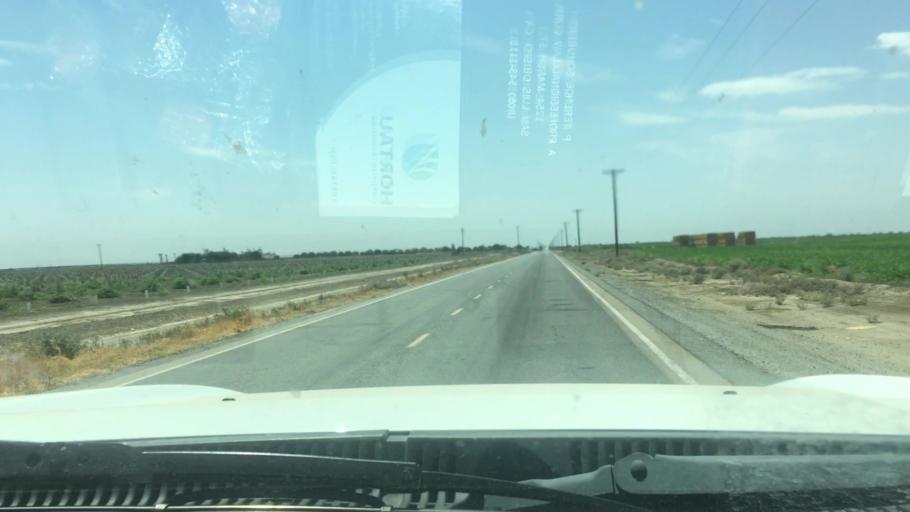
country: US
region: California
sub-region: Tulare County
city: Tipton
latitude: 36.0510
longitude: -119.4340
